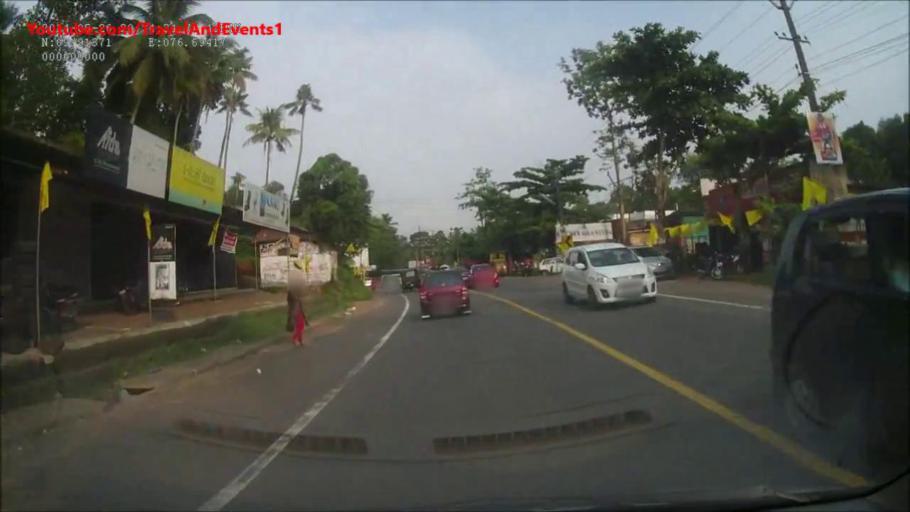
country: IN
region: Kerala
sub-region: Ernakulam
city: Muvattupula
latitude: 9.9144
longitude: 76.6927
